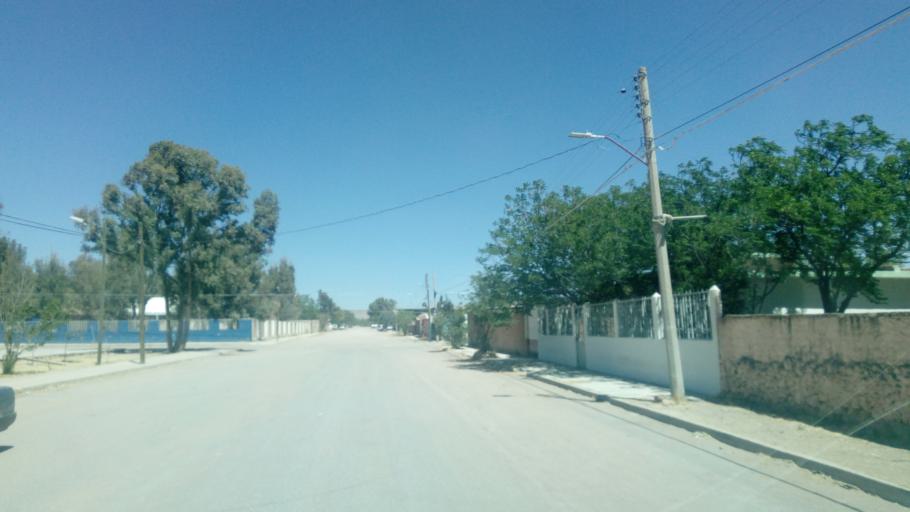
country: MX
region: Durango
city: Victoria de Durango
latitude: 24.0759
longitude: -104.6557
